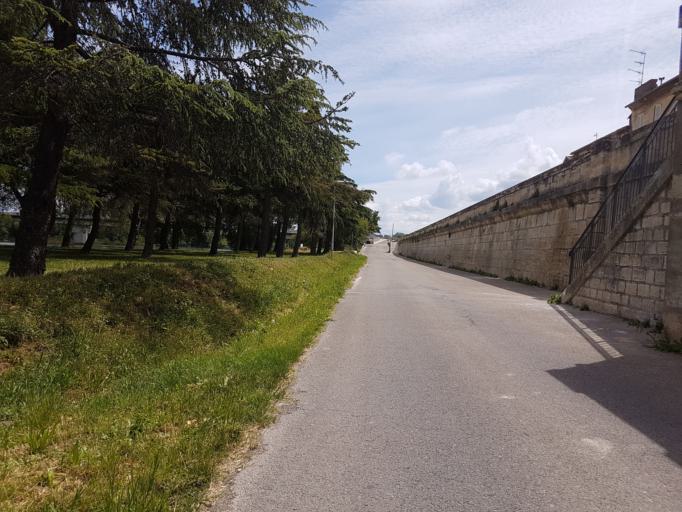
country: FR
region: Languedoc-Roussillon
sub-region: Departement du Gard
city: Beaucaire
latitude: 43.8068
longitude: 4.6484
